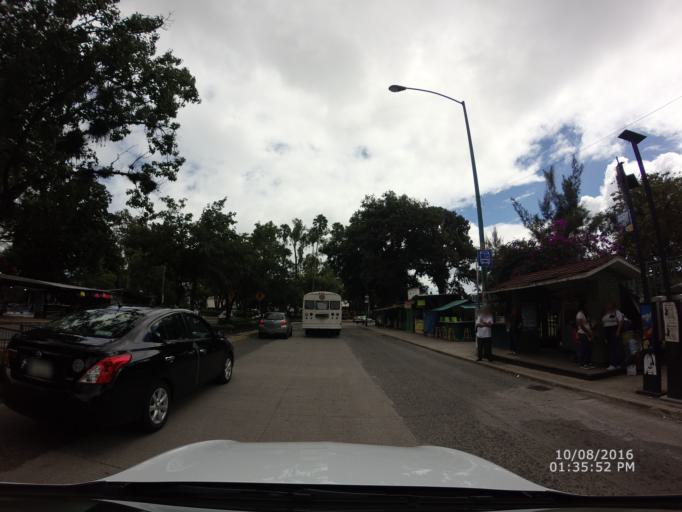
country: MX
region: Veracruz
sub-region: Xalapa
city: Xalapa de Enriquez
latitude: 19.5252
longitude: -96.9332
